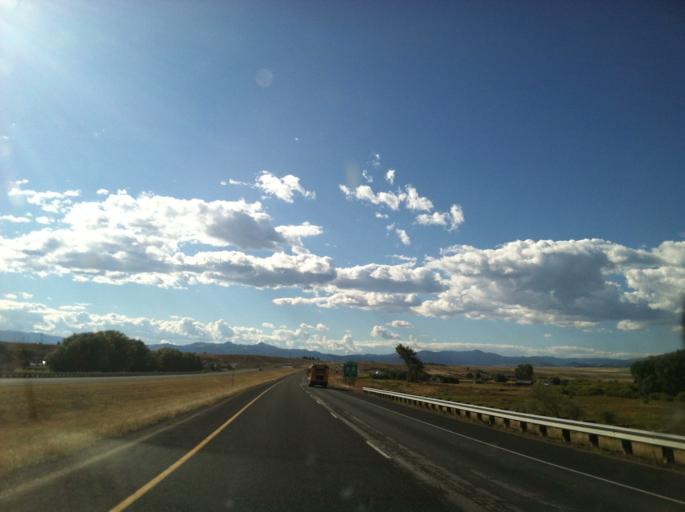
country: US
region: Montana
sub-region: Jefferson County
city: Whitehall
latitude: 45.8769
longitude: -112.0937
